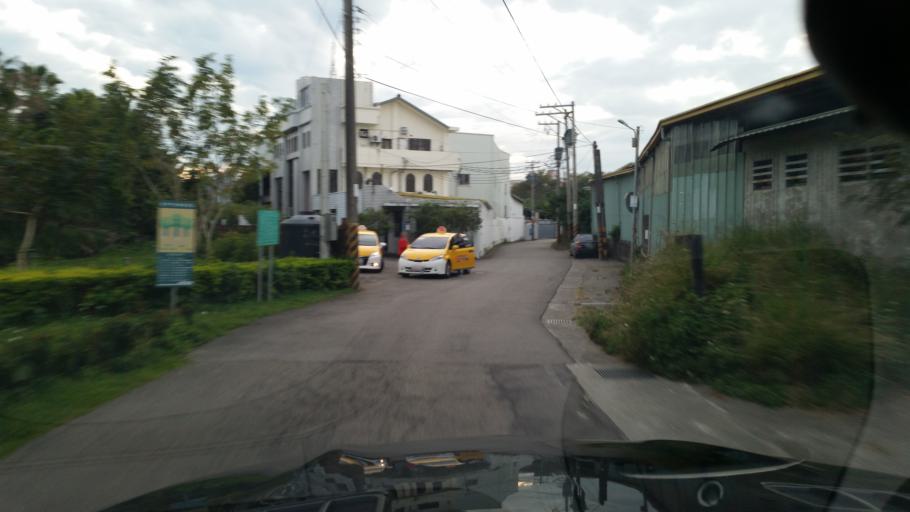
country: TW
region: Taiwan
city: Fengyuan
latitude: 24.2035
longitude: 120.7131
